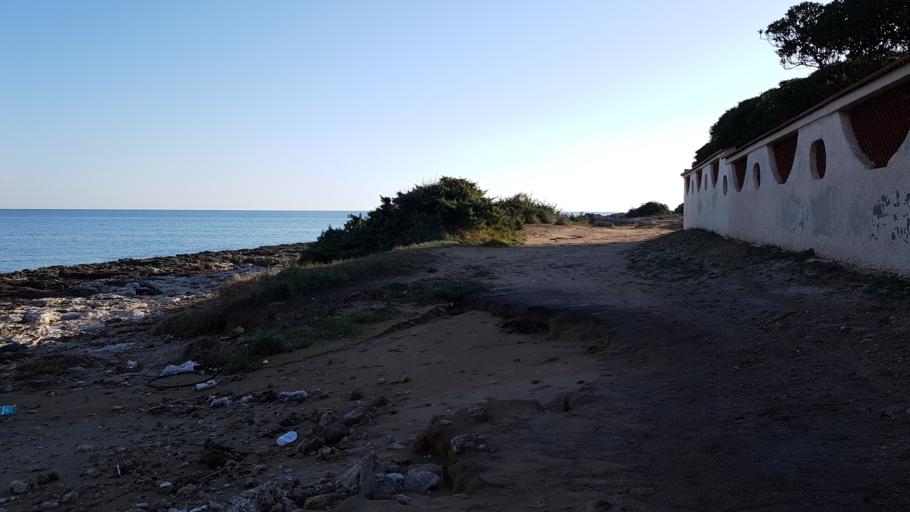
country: IT
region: Apulia
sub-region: Provincia di Taranto
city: Avetrana
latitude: 40.2942
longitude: 17.7667
